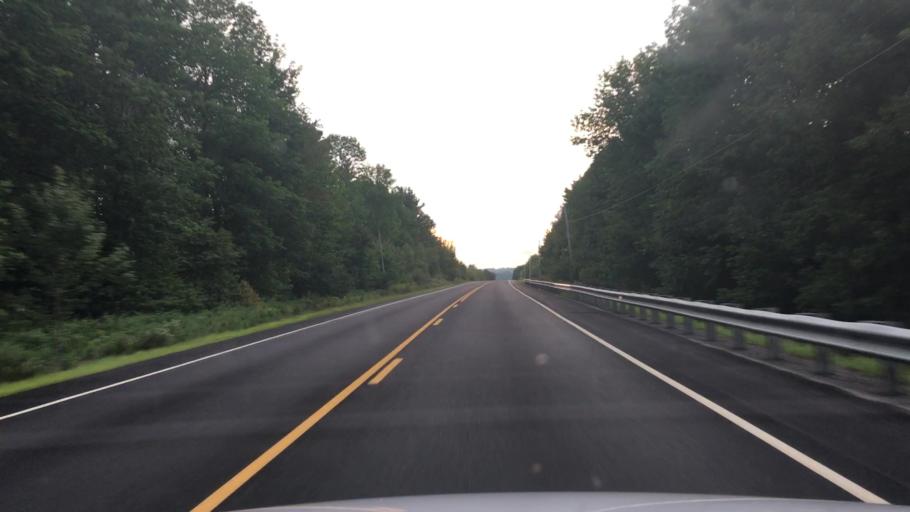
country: US
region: Maine
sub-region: Waldo County
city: Searsmont
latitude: 44.4004
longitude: -69.2524
